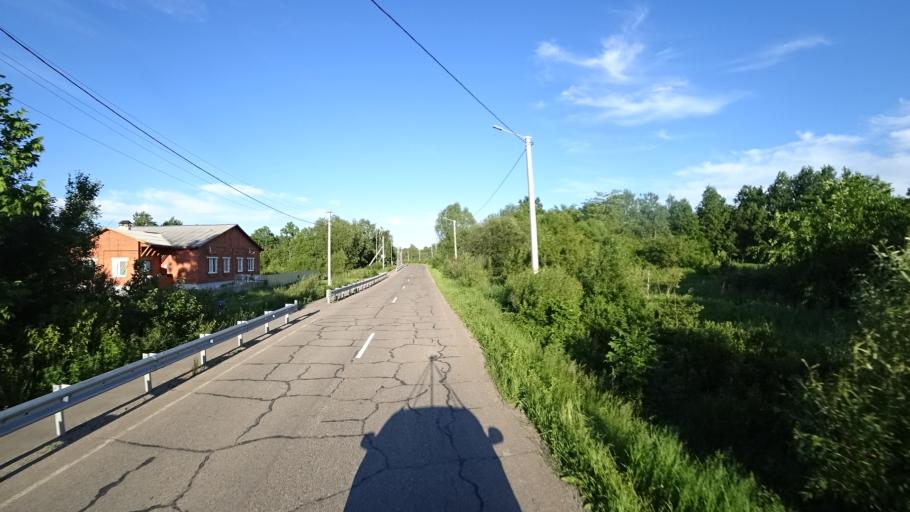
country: RU
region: Khabarovsk Krai
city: Khor
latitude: 47.8535
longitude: 134.9748
